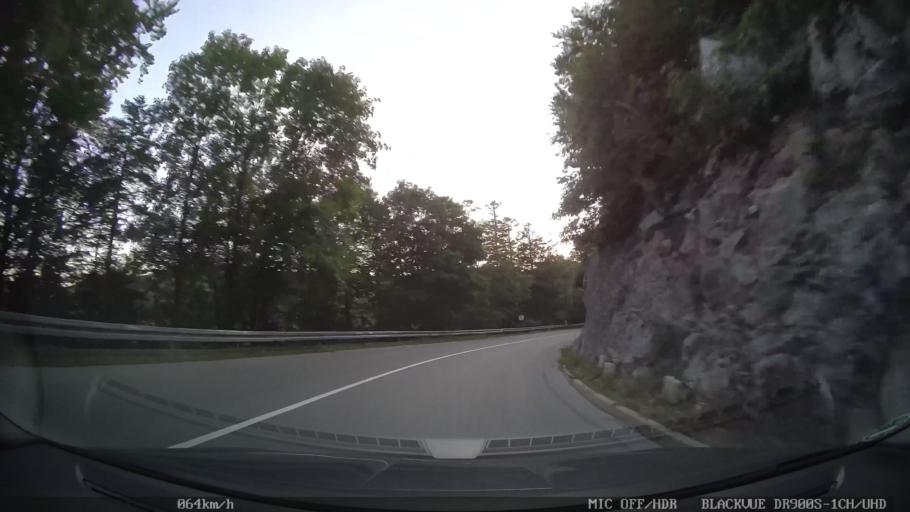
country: HR
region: Primorsko-Goranska
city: Novi Vinodolski
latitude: 45.1637
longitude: 14.9379
